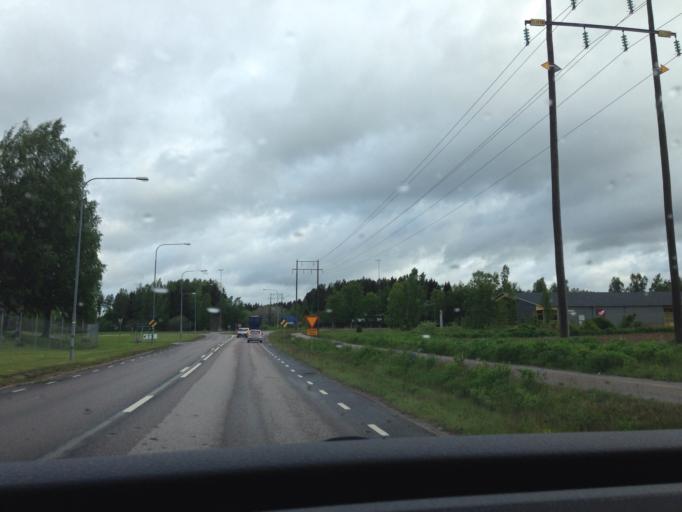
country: SE
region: Vaestra Goetaland
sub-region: Tibro Kommun
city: Tibro
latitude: 58.4192
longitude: 14.1314
